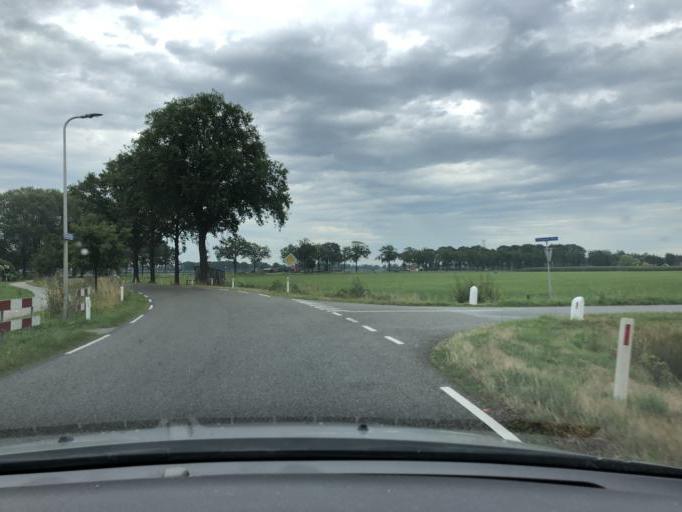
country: NL
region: Overijssel
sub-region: Gemeente Dalfsen
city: Dalfsen
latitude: 52.5608
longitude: 6.2998
